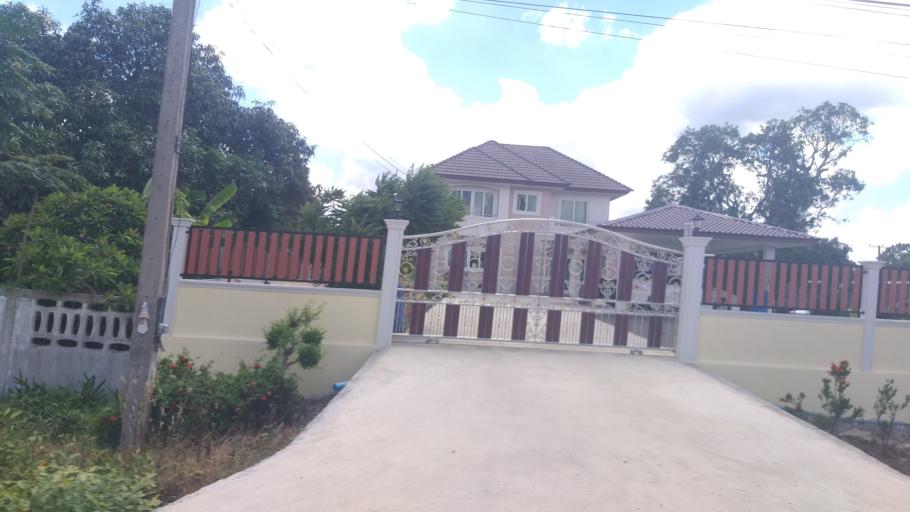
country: TH
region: Sara Buri
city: Wihan Daeng
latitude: 14.3933
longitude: 101.0968
